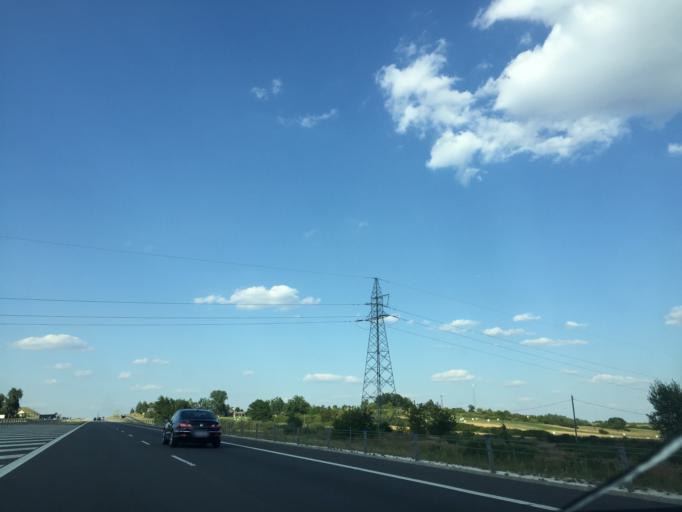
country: PL
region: Swietokrzyskie
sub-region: Powiat kielecki
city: Checiny
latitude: 50.7849
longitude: 20.4710
